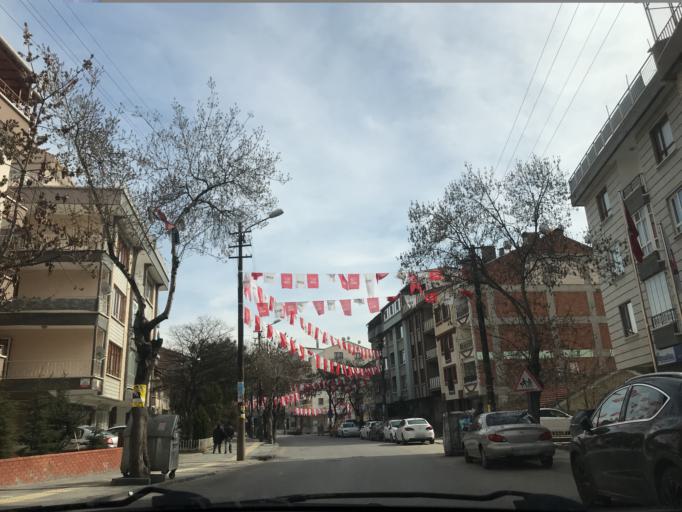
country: TR
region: Ankara
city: Batikent
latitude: 39.9666
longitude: 32.7998
